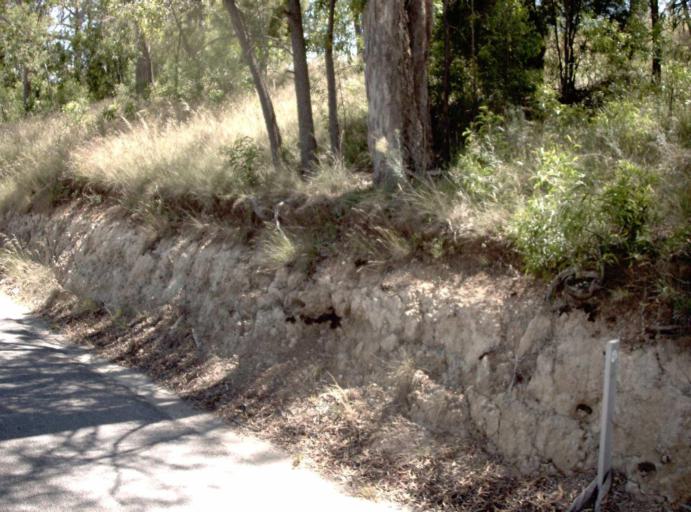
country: AU
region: Victoria
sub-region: East Gippsland
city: Lakes Entrance
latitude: -37.4550
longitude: 148.1934
